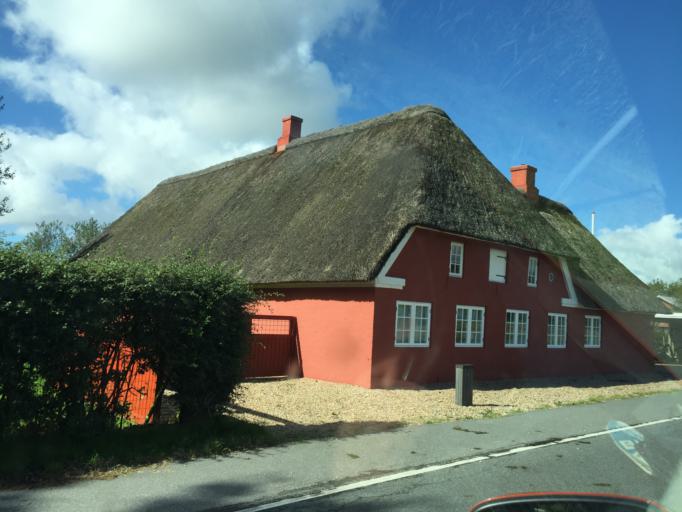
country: DK
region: South Denmark
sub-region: Esbjerg Kommune
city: Bramming
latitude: 55.4263
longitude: 8.6471
